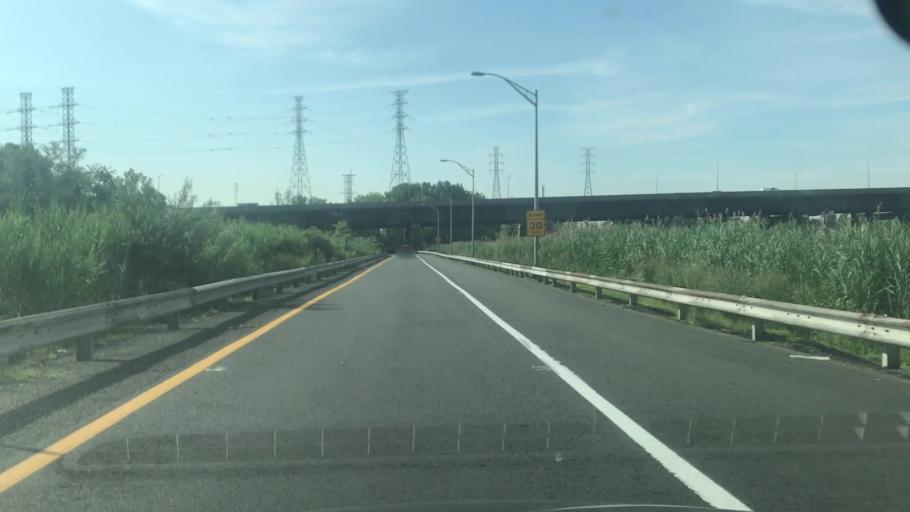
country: US
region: New Jersey
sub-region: Hudson County
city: Kearny
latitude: 40.7521
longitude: -74.1178
